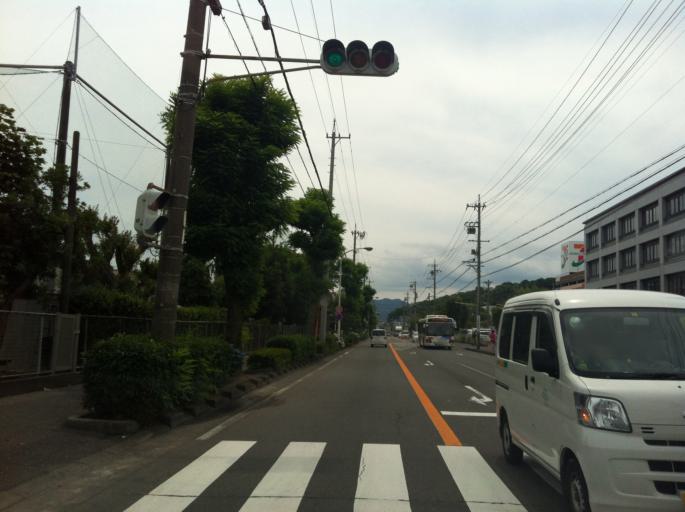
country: JP
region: Shizuoka
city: Shizuoka-shi
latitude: 34.9724
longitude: 138.4099
